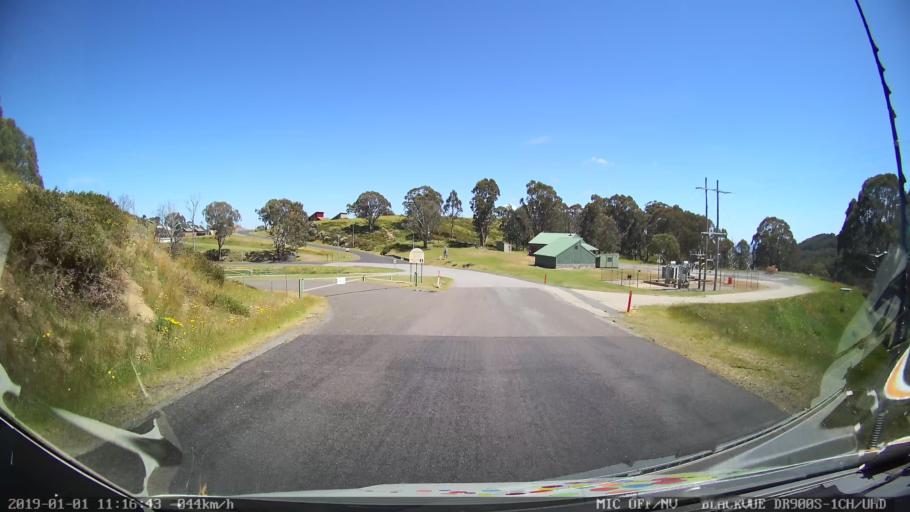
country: AU
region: New South Wales
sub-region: Snowy River
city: Jindabyne
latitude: -35.9375
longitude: 148.3852
